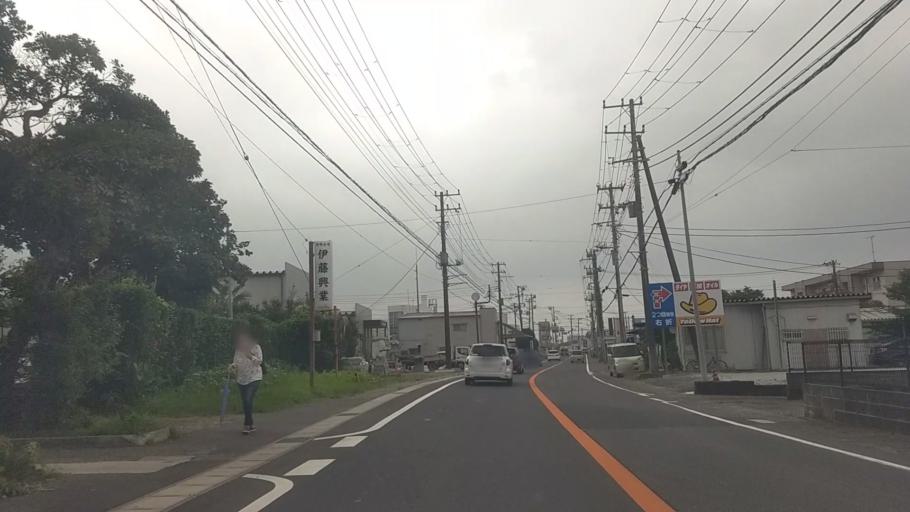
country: JP
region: Chiba
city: Kawaguchi
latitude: 35.1127
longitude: 140.0958
